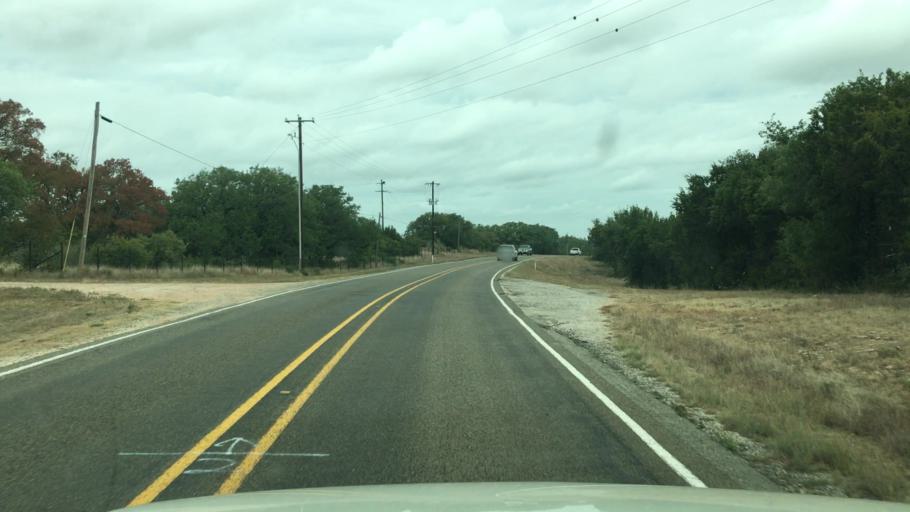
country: US
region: Texas
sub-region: Llano County
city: Horseshoe Bay
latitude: 30.4651
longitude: -98.4100
